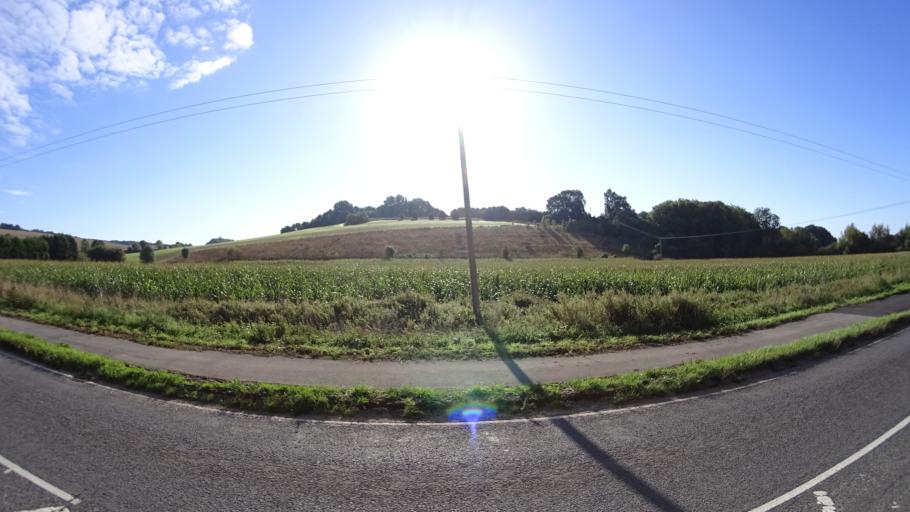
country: GB
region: England
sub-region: Hampshire
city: Romsey
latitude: 51.0363
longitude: -1.5257
